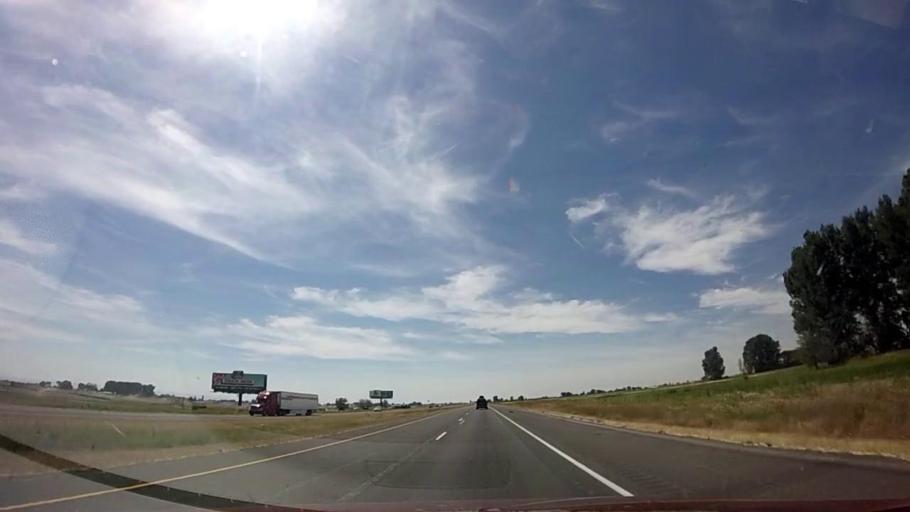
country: US
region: Idaho
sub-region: Minidoka County
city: Heyburn
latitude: 42.5692
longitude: -113.7070
